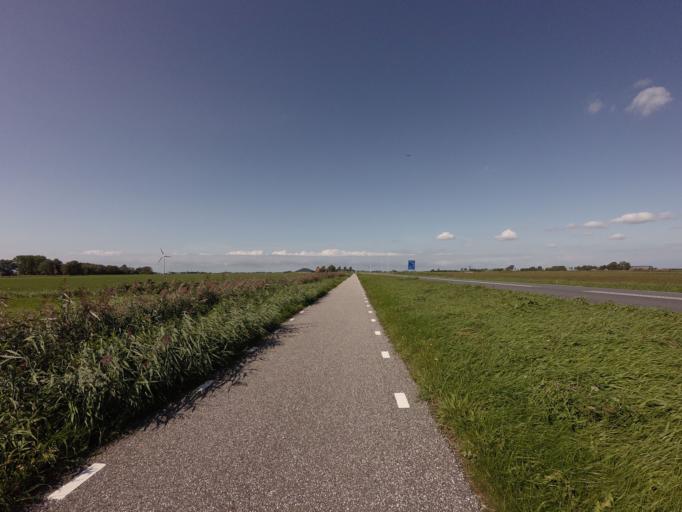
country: NL
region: Friesland
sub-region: Gemeente Littenseradiel
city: Makkum
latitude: 53.1129
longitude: 5.6840
